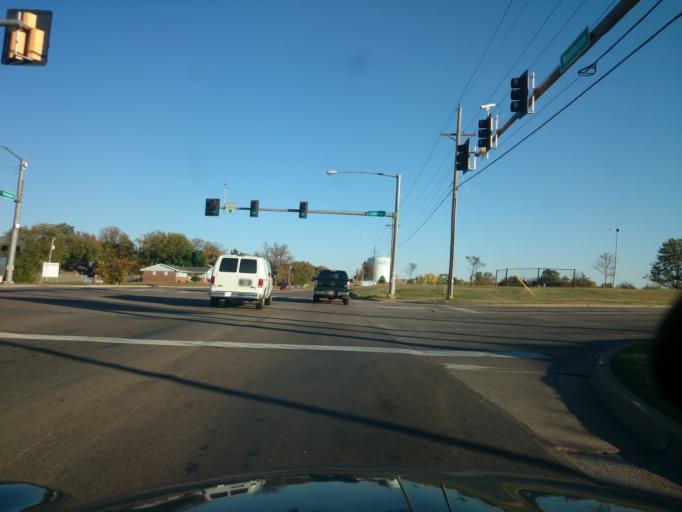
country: US
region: Oklahoma
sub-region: Payne County
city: Stillwater
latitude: 36.1449
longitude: -97.0695
